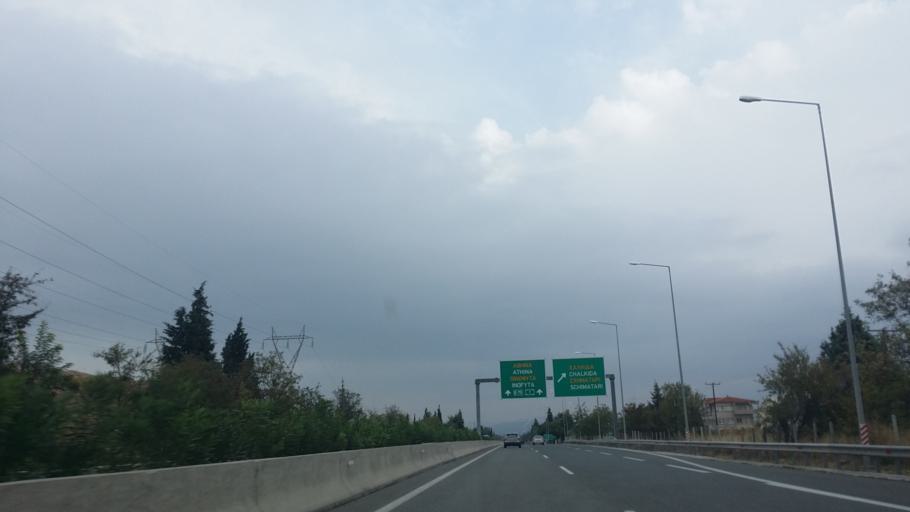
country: GR
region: Central Greece
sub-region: Nomos Voiotias
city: Schimatari
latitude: 38.3574
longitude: 23.5640
